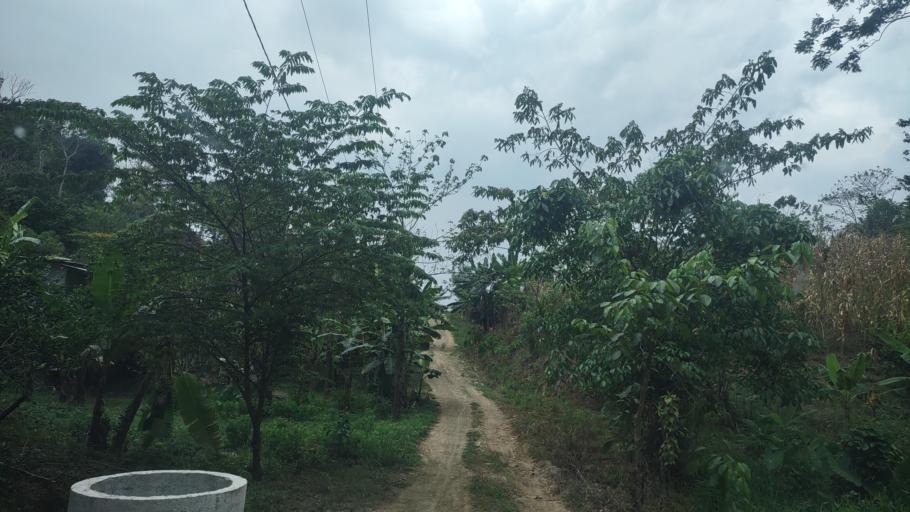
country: MX
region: Veracruz
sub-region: Uxpanapa
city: Poblado 10
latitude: 17.4531
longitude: -94.1005
